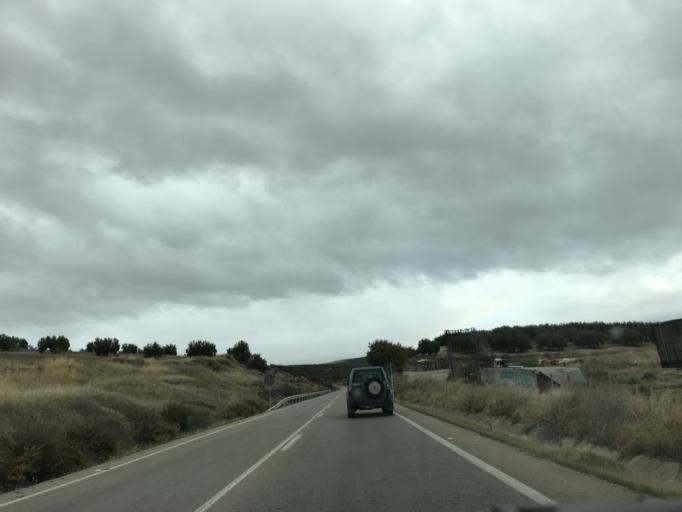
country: ES
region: Andalusia
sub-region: Provincia de Jaen
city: Peal de Becerro
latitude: 37.9225
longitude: -3.1340
